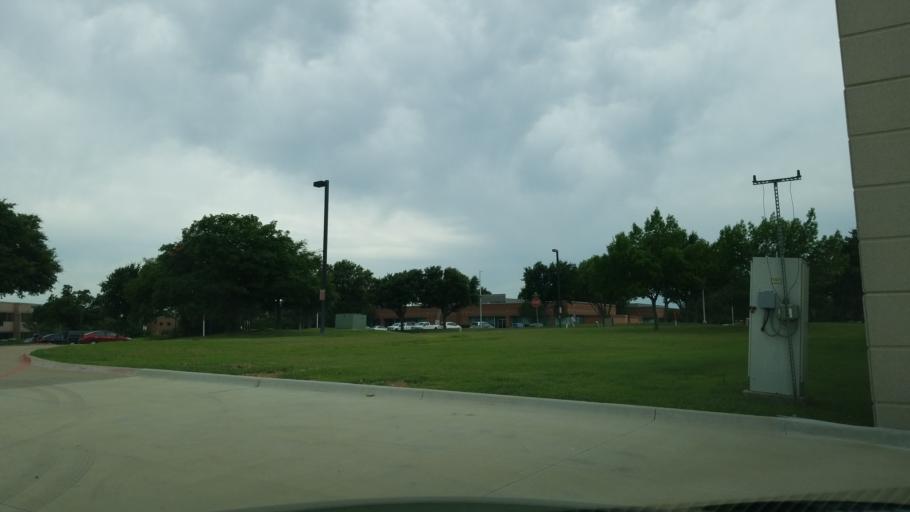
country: US
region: Texas
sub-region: Dallas County
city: Coppell
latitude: 32.8952
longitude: -96.9837
